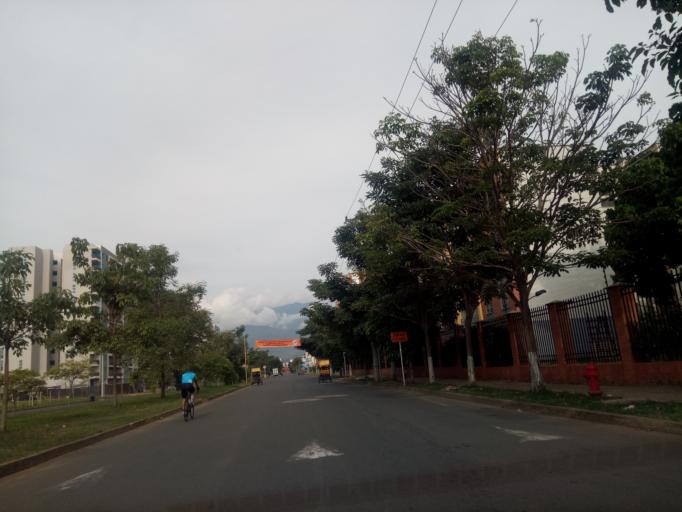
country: CO
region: Valle del Cauca
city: Cali
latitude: 3.3684
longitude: -76.5143
